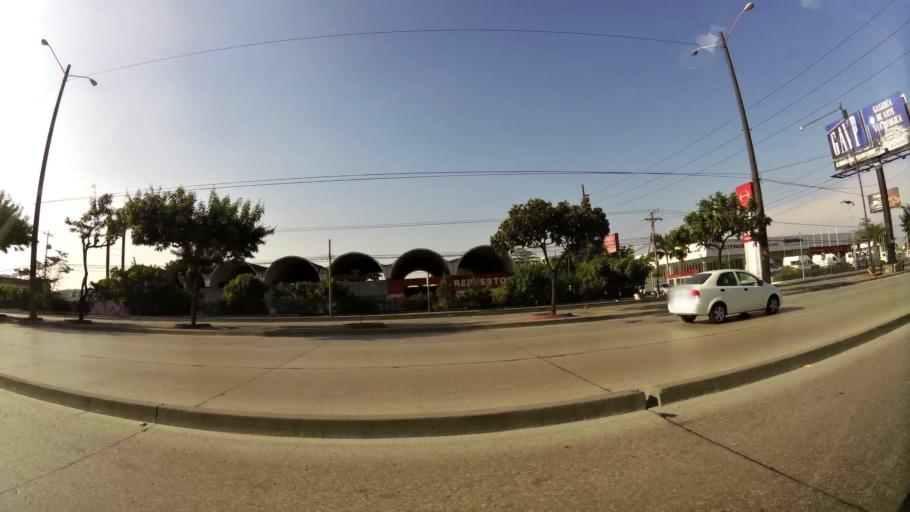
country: EC
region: Guayas
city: Guayaquil
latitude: -2.1467
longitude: -79.9131
